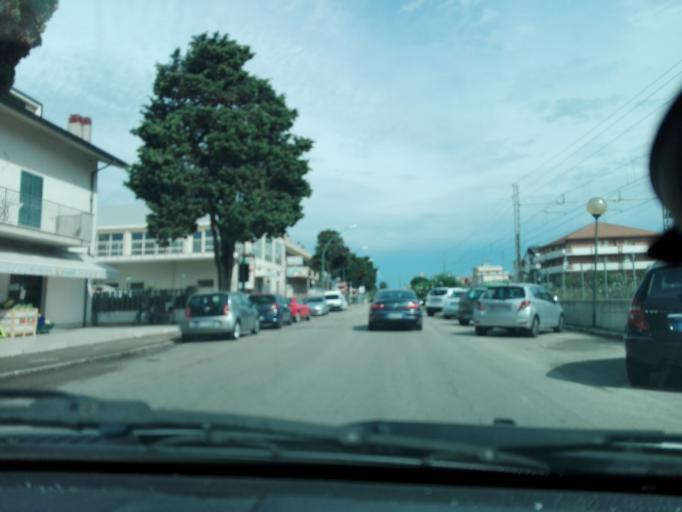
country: IT
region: Abruzzo
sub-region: Provincia di Teramo
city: Pineto
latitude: 42.6148
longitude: 14.0623
